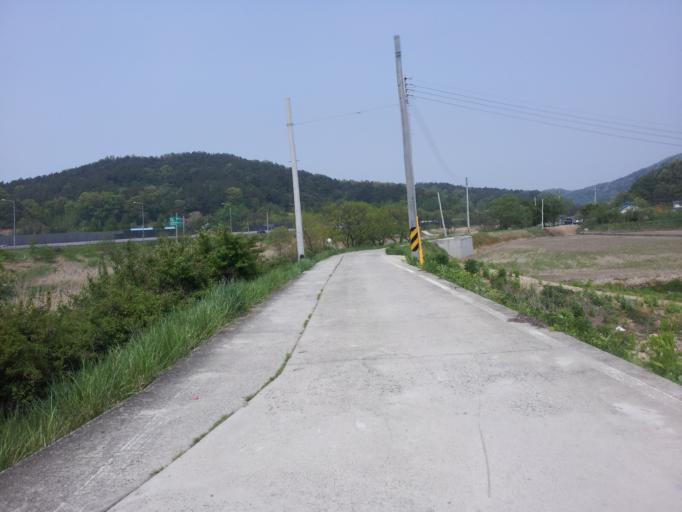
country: KR
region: Daejeon
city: Daejeon
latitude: 36.2576
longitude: 127.2826
